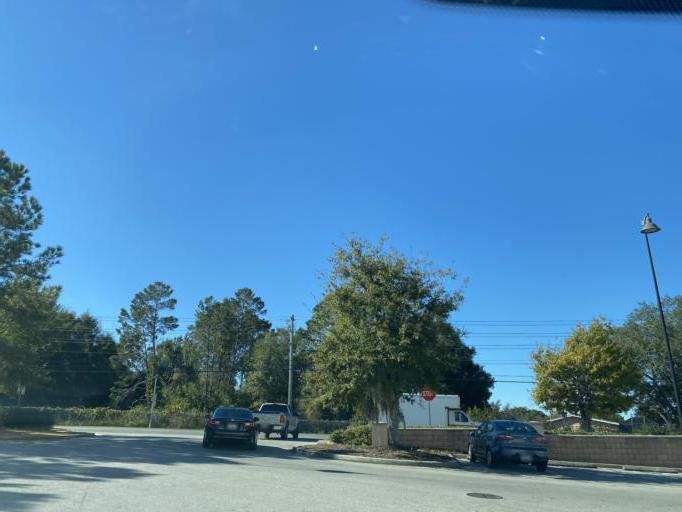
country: US
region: Florida
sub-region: Lake County
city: Lady Lake
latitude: 28.9313
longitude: -81.9365
